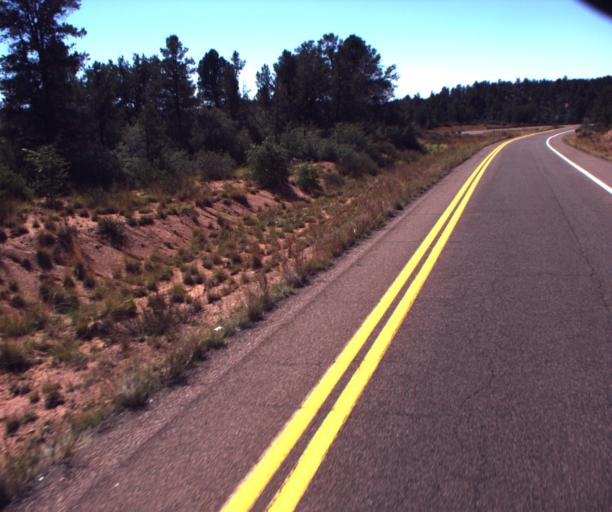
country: US
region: Arizona
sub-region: Gila County
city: Star Valley
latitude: 34.2695
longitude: -111.1865
